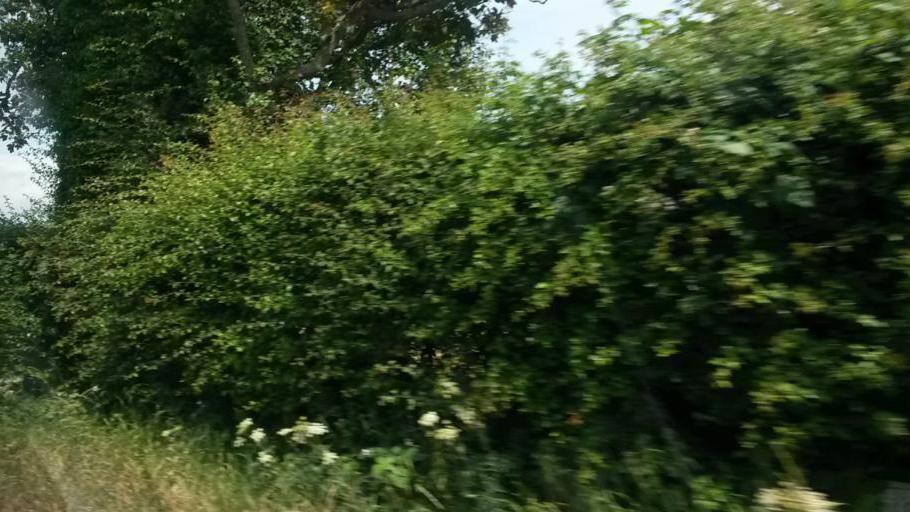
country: IE
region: Leinster
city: Lusk
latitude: 53.5443
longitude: -6.2044
